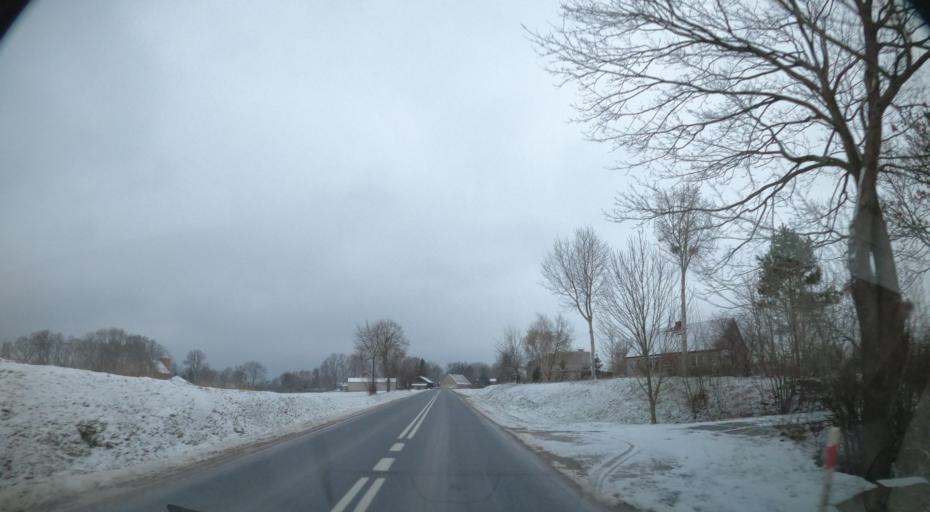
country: PL
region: Masovian Voivodeship
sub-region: Powiat plocki
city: Nowy Duninow
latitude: 52.6132
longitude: 19.4641
